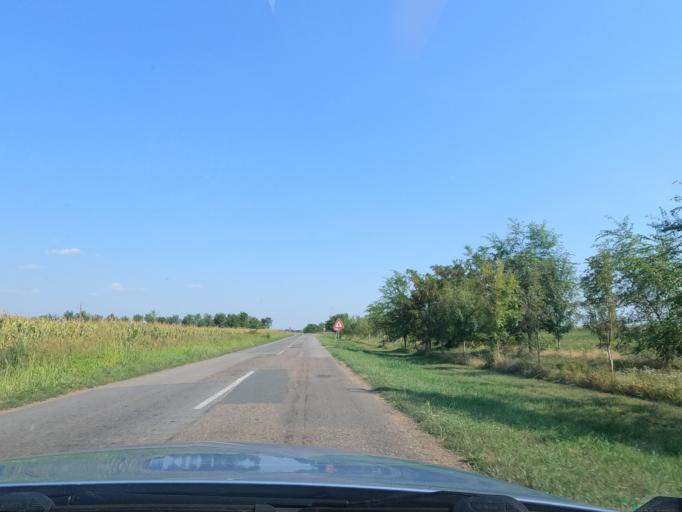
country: RS
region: Autonomna Pokrajina Vojvodina
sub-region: Juznobacki Okrug
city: Becej
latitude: 45.6425
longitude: 19.9926
